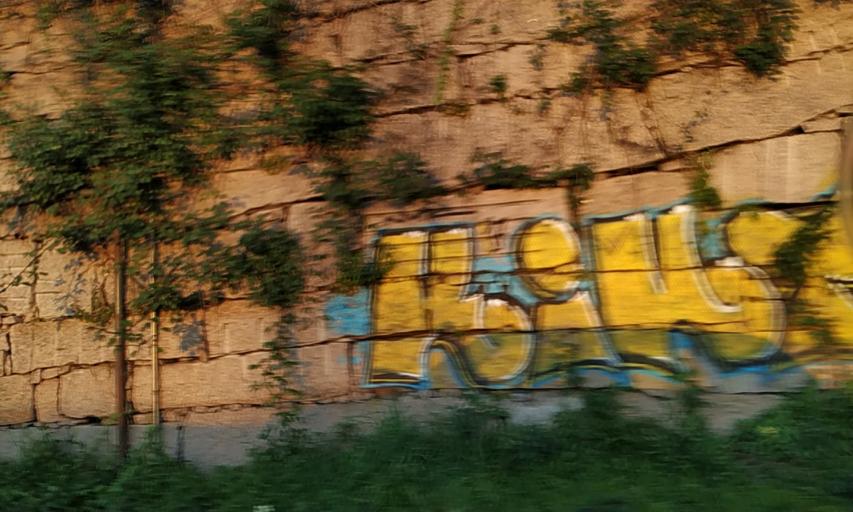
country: ES
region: Galicia
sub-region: Provincia de Pontevedra
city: Vigo
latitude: 42.2401
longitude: -8.7085
